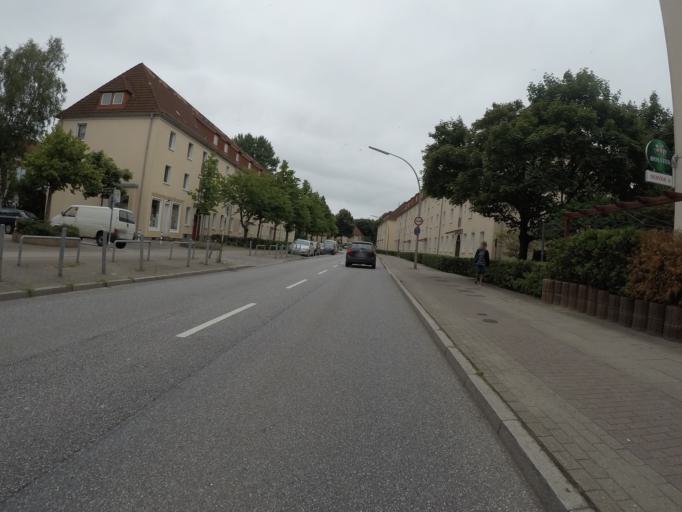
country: DE
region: Hamburg
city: Altona
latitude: 53.5294
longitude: 9.8788
